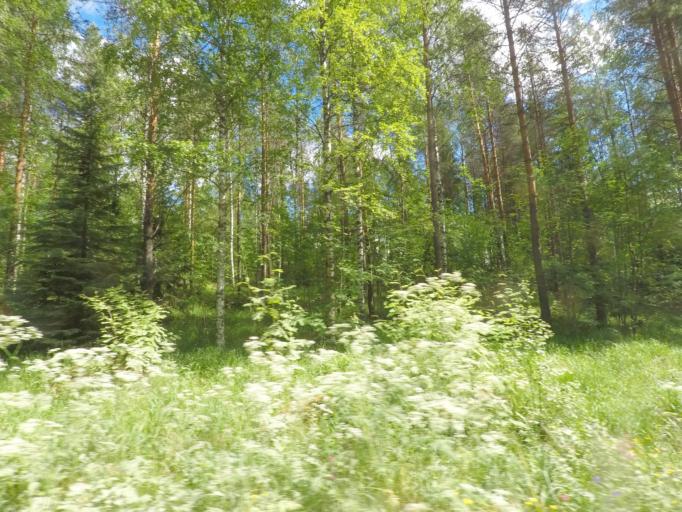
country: FI
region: Central Finland
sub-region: Jyvaeskylae
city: Hankasalmi
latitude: 62.4323
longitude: 26.6484
